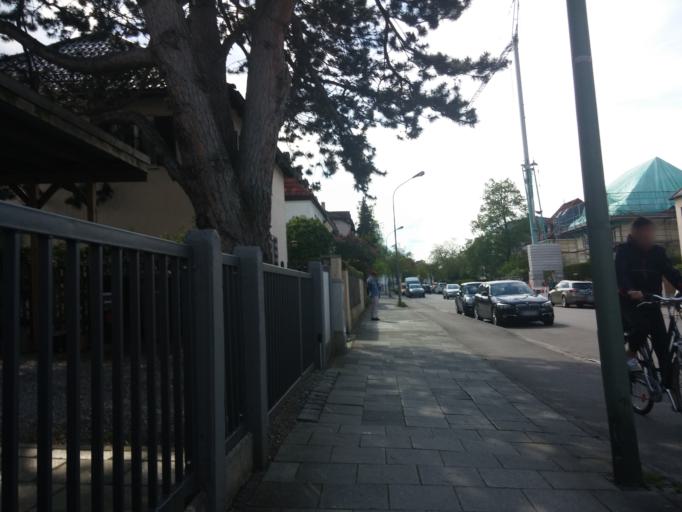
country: DE
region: Bavaria
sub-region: Upper Bavaria
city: Munich
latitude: 48.1172
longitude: 11.5247
